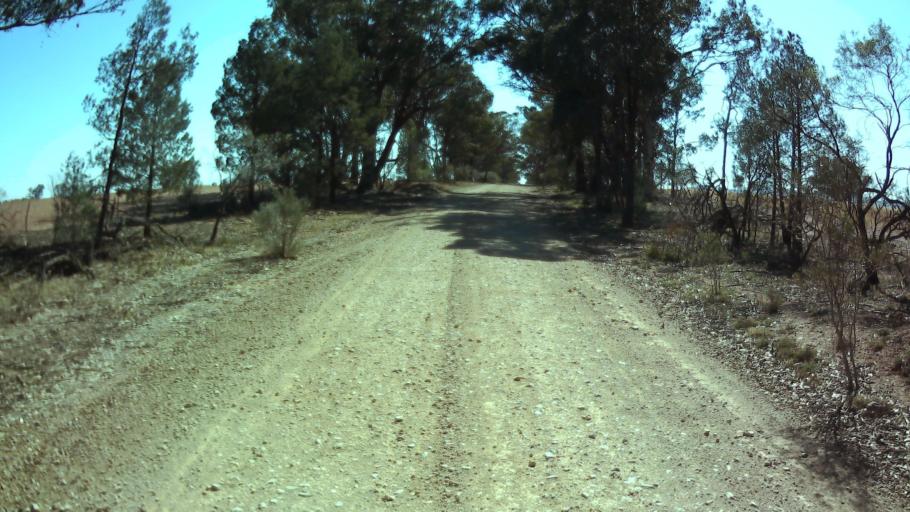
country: AU
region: New South Wales
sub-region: Weddin
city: Grenfell
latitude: -33.9061
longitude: 147.8546
